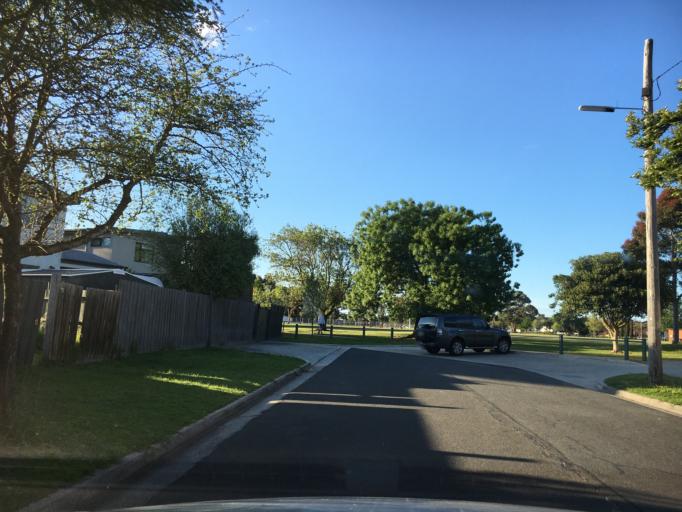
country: AU
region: Victoria
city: Clayton
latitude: -37.9107
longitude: 145.1172
